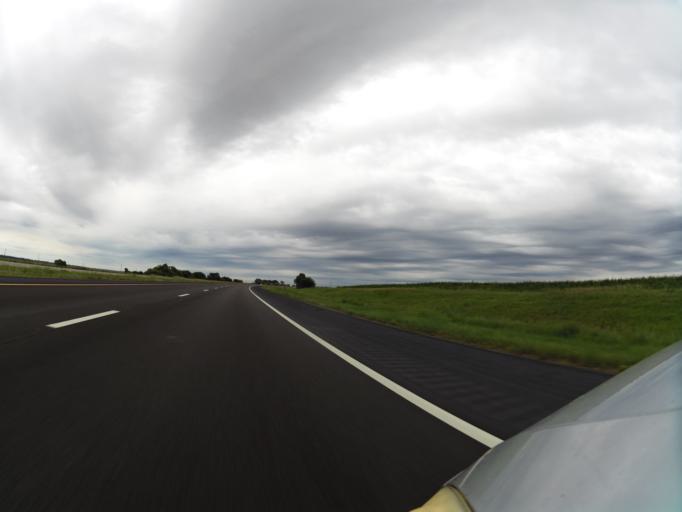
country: US
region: Kansas
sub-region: Sedgwick County
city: Colwich
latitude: 37.8419
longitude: -97.5776
